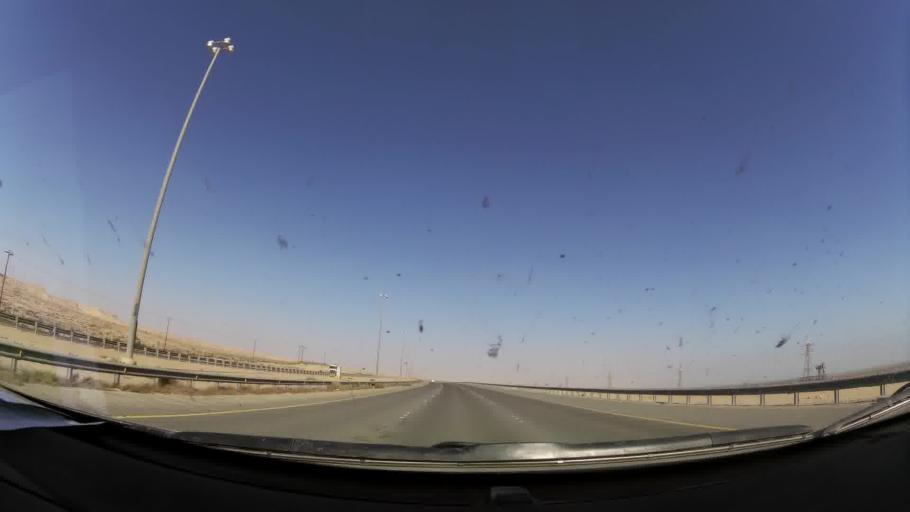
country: KW
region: Muhafazat al Jahra'
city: Al Jahra'
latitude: 29.4962
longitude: 47.7912
